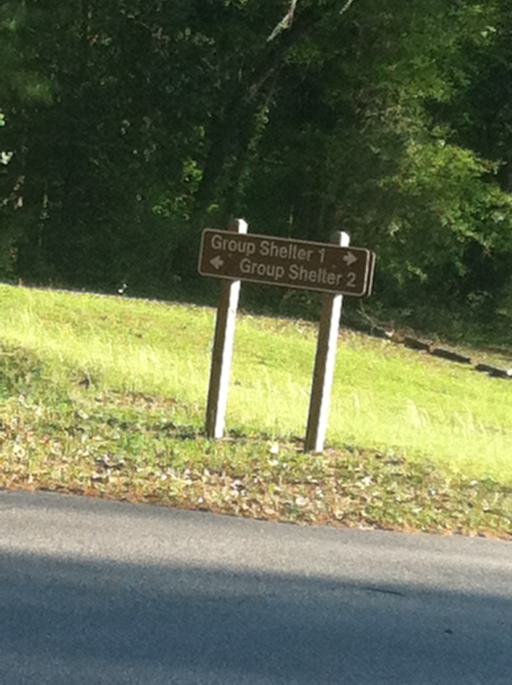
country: US
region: Georgia
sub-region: Early County
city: Blakely
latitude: 31.4698
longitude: -84.9363
